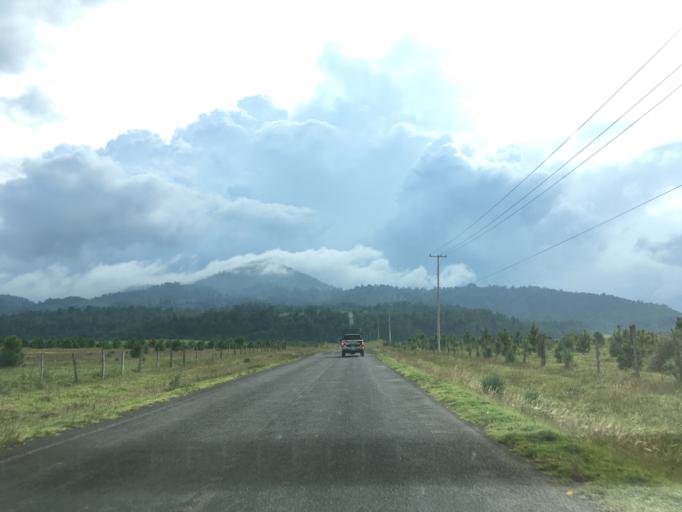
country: MX
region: Michoacan
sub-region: Nahuatzen
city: Sevina
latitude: 19.6159
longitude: -101.8551
